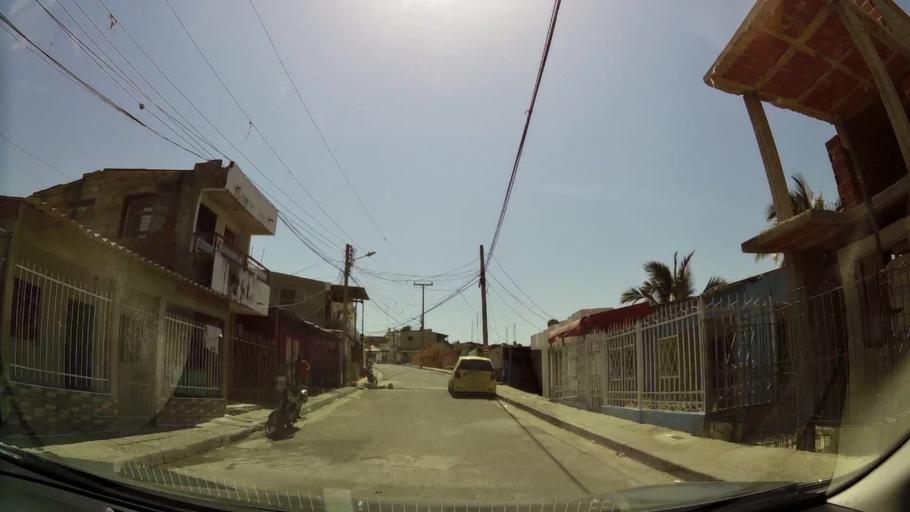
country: CO
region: Bolivar
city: Cartagena
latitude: 10.4327
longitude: -75.5260
